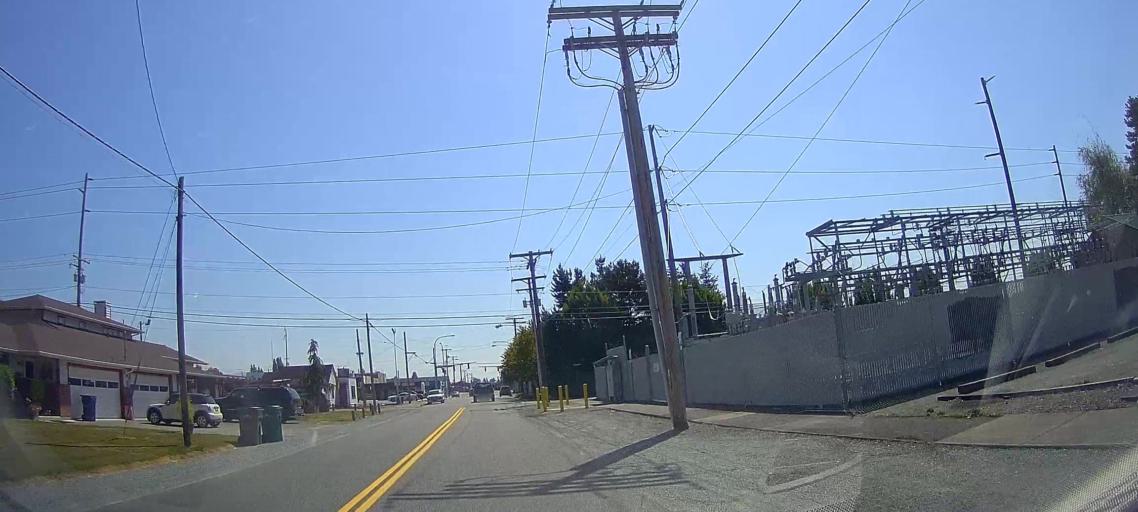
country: US
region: Washington
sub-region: Skagit County
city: Burlington
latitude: 48.4768
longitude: -122.3308
